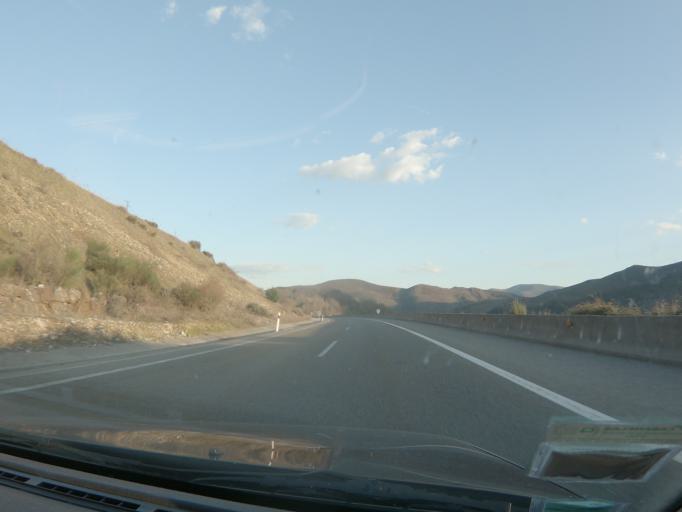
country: ES
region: Castille and Leon
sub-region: Provincia de Leon
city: Vega de Valcarce
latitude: 42.6725
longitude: -6.9592
